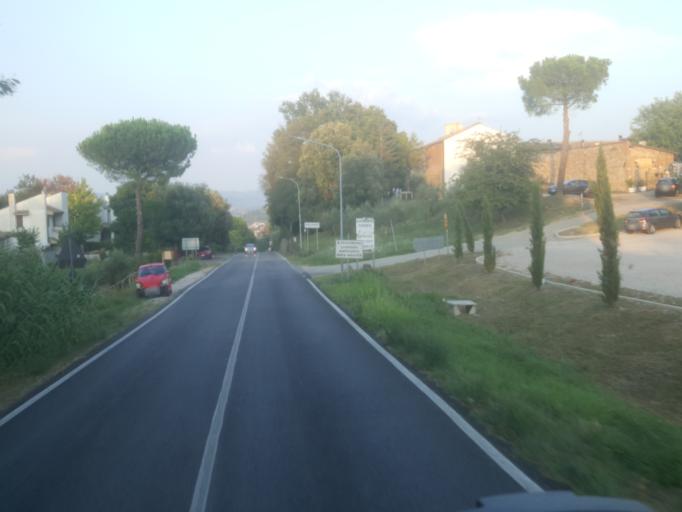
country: IT
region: Tuscany
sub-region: Province of Florence
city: Certaldo
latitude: 43.5442
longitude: 11.0149
